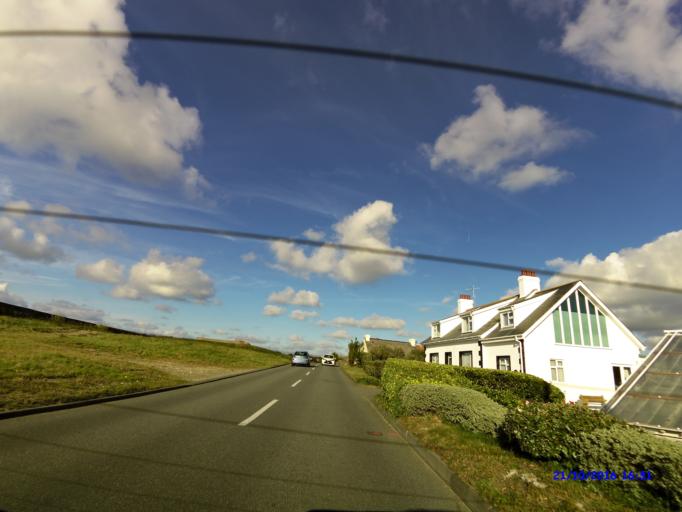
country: GG
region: St Peter Port
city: Saint Peter Port
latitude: 49.4428
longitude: -2.6497
